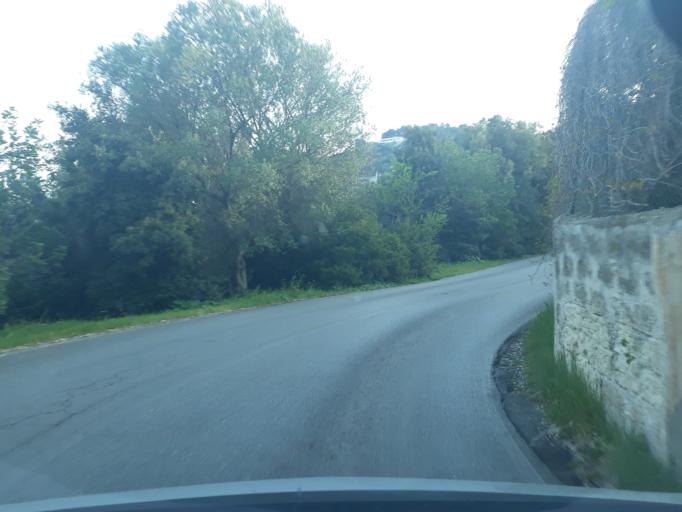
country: IT
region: Apulia
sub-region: Provincia di Brindisi
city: Lamie di Olimpie-Selva
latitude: 40.8312
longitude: 17.3411
